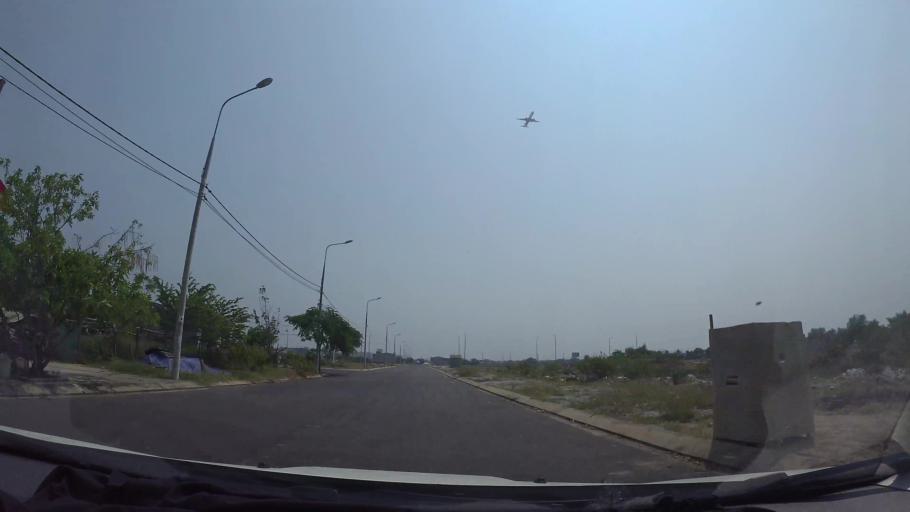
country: VN
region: Da Nang
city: Cam Le
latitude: 15.9788
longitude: 108.2116
